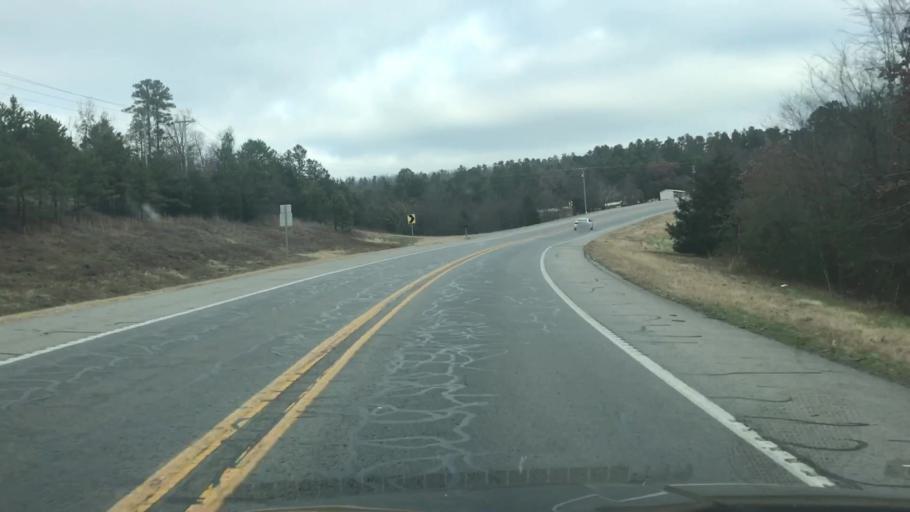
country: US
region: Arkansas
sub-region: Scott County
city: Waldron
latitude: 34.8111
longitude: -94.0403
